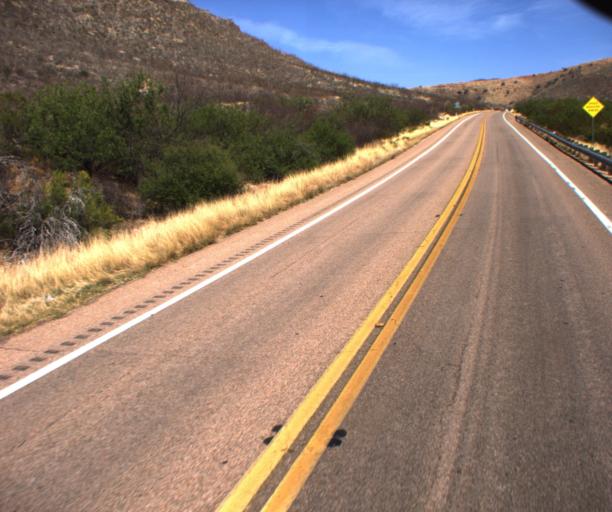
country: US
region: Arizona
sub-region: Cochise County
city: Bisbee
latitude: 31.5174
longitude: -110.0260
